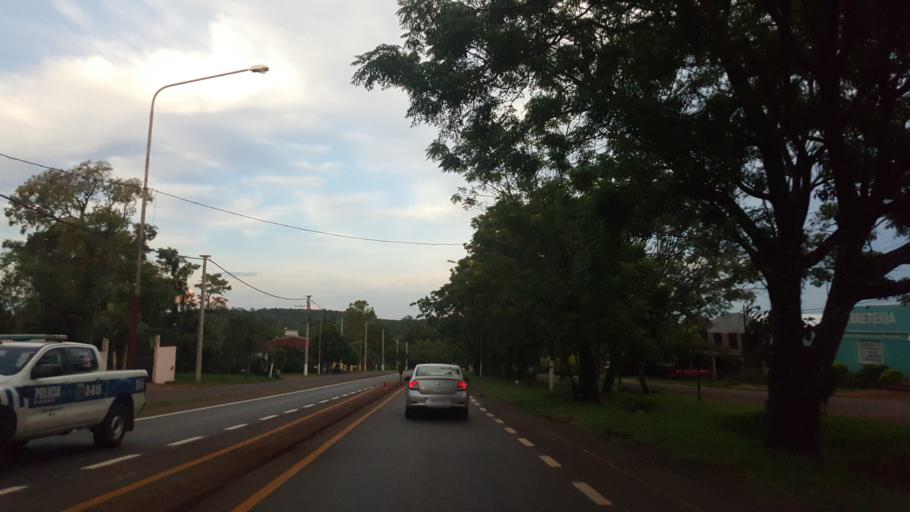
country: AR
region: Misiones
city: Jardin America
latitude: -27.0349
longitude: -55.2249
